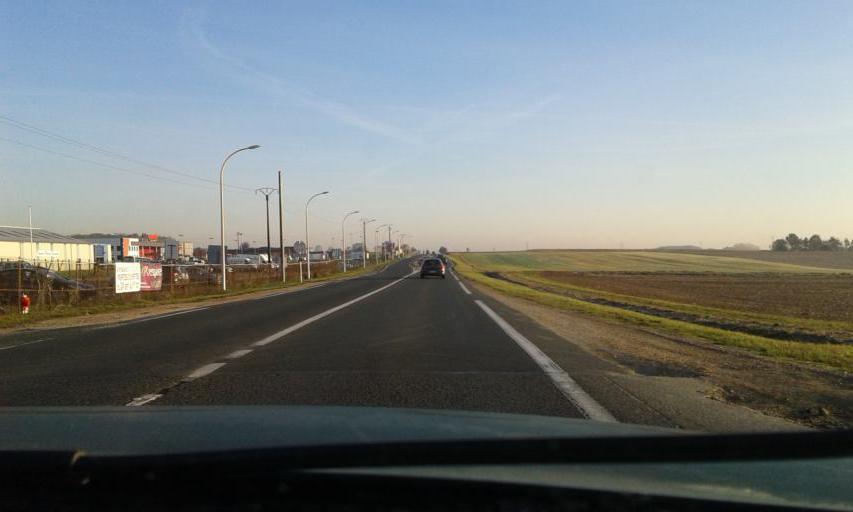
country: FR
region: Centre
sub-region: Departement du Loiret
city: Beaugency
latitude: 47.7892
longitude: 1.6428
